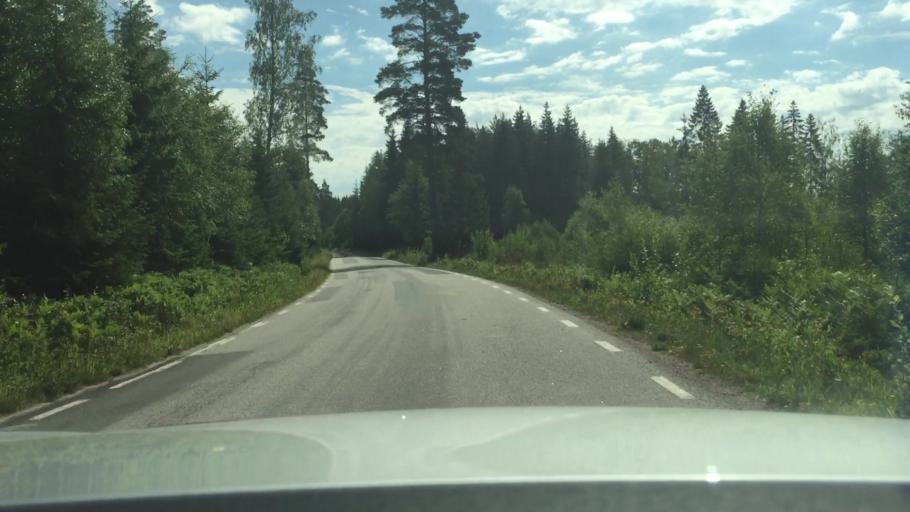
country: SE
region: Vaestra Goetaland
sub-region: Tidaholms Kommun
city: Olofstorp
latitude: 58.3421
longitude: 14.0162
